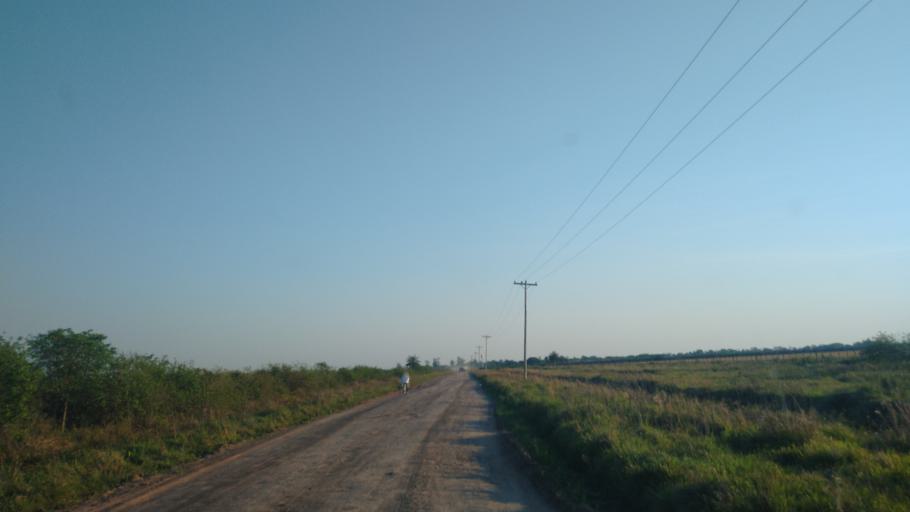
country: PY
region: Neembucu
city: Cerrito
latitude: -27.3858
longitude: -57.6574
